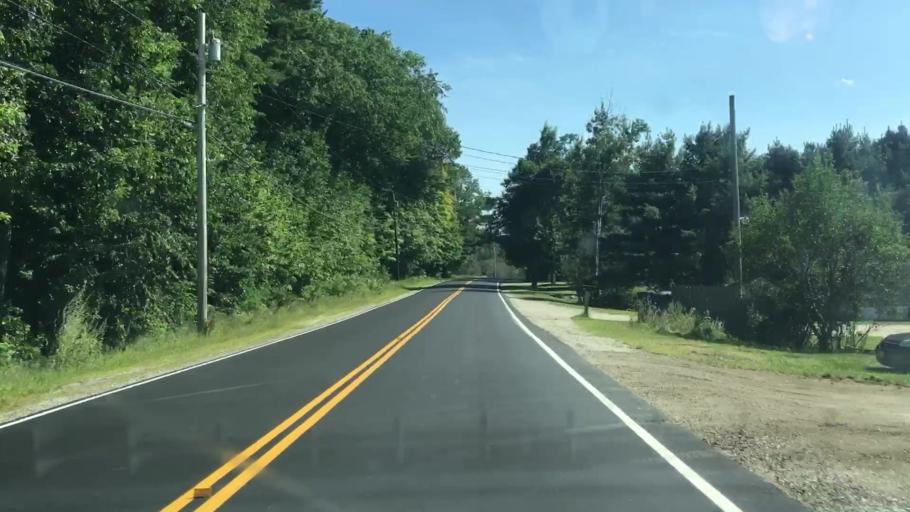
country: US
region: Maine
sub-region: Androscoggin County
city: Sabattus
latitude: 44.1301
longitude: -70.0873
